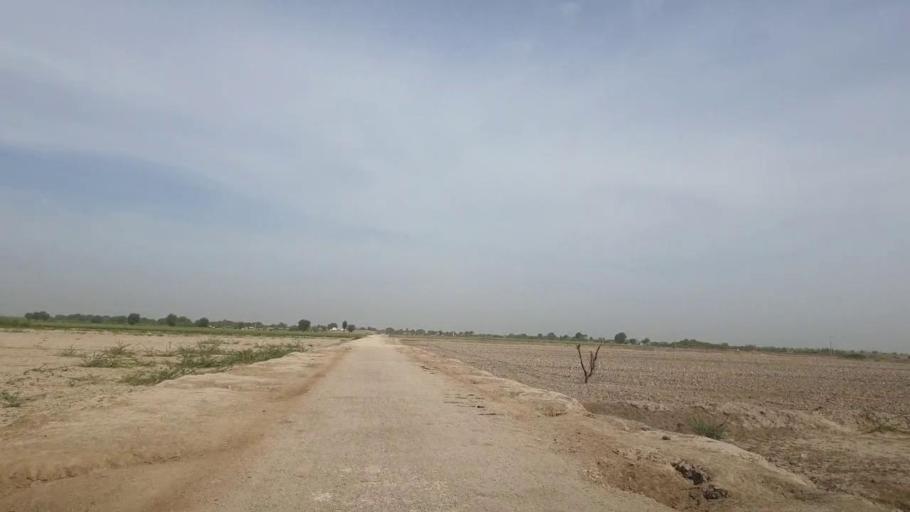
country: PK
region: Sindh
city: Kunri
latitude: 25.1721
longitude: 69.6175
